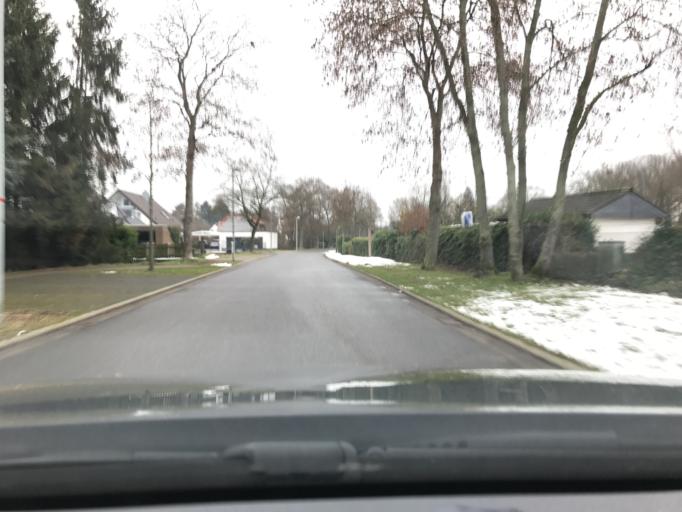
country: DE
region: North Rhine-Westphalia
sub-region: Regierungsbezirk Dusseldorf
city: Krefeld
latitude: 51.3504
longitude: 6.5644
